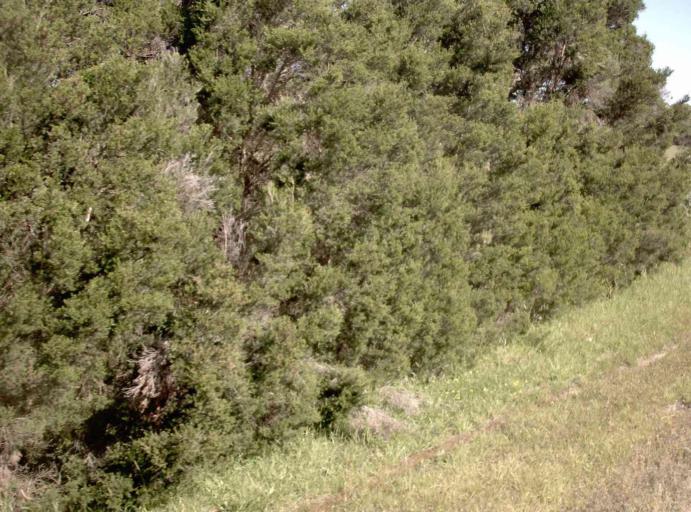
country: AU
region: Victoria
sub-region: Latrobe
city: Traralgon
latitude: -38.6415
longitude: 146.6712
